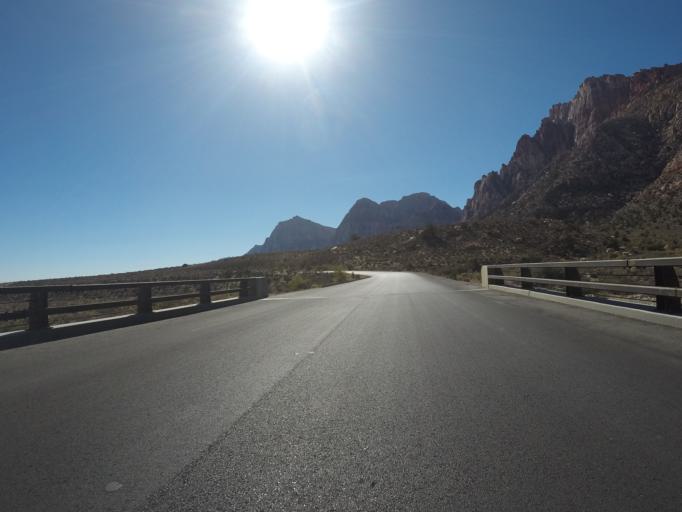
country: US
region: Nevada
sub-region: Clark County
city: Summerlin South
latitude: 36.1447
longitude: -115.4766
